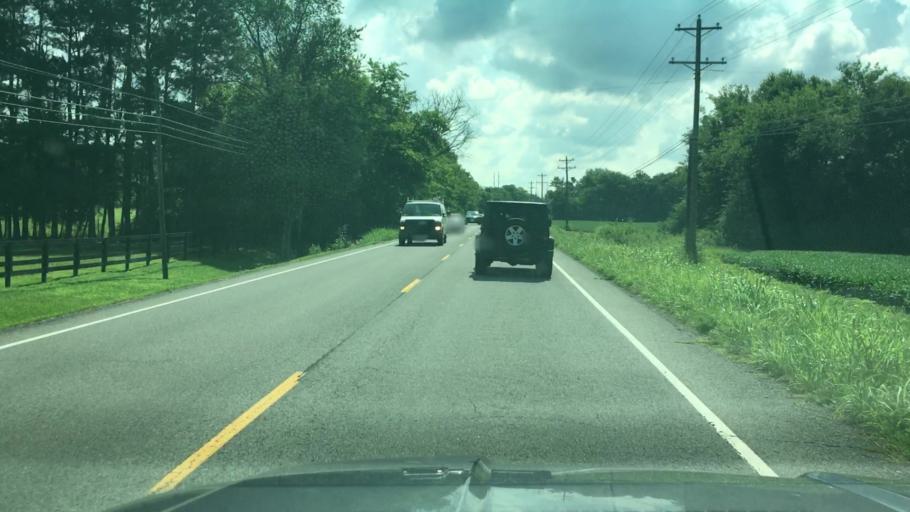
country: US
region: Tennessee
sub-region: Williamson County
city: Nolensville
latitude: 35.8679
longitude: -86.7053
